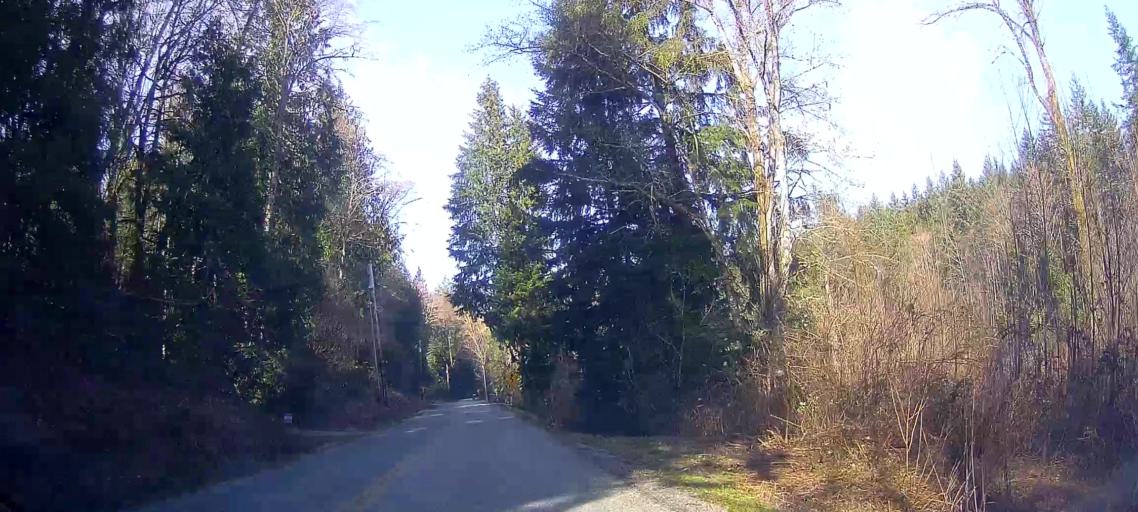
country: US
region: Washington
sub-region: Whatcom County
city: Sudden Valley
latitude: 48.6216
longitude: -122.3694
